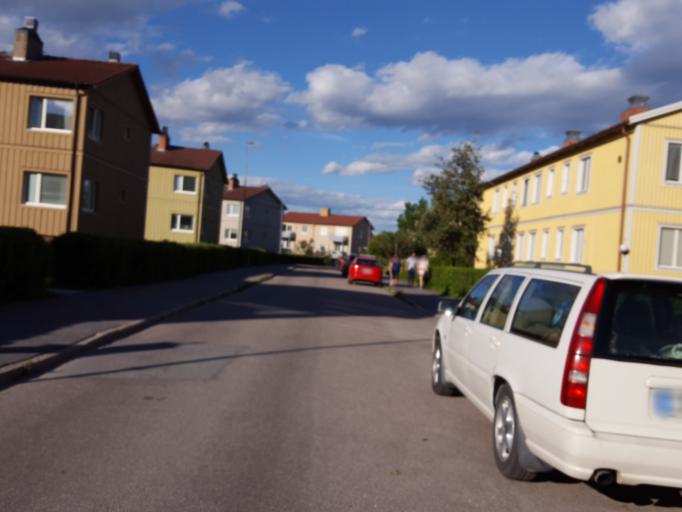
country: SE
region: Uppsala
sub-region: Uppsala Kommun
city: Uppsala
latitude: 59.8620
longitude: 17.6567
